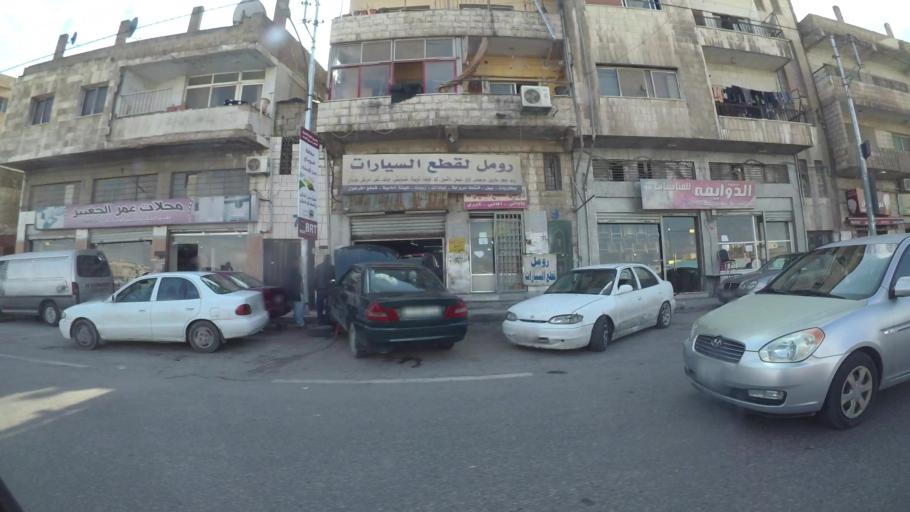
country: JO
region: Amman
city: Al Jubayhah
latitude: 32.0211
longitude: 35.8420
